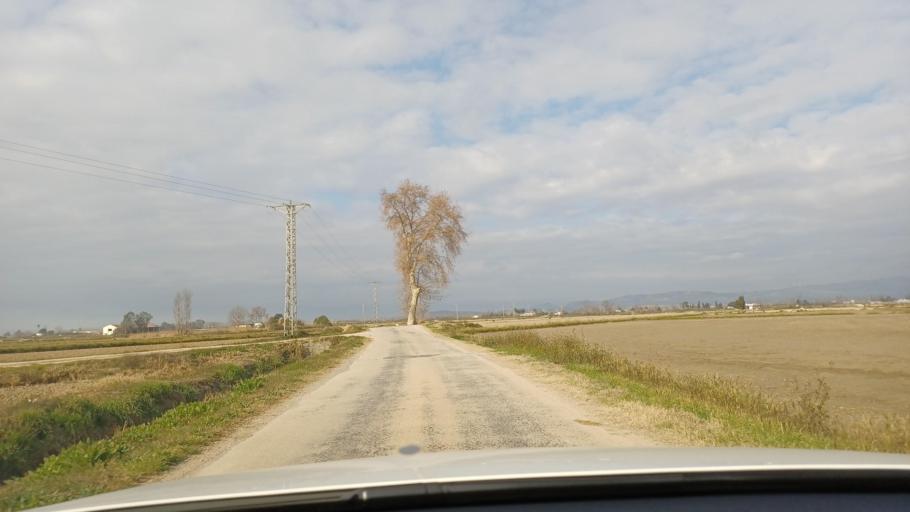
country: ES
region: Catalonia
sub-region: Provincia de Tarragona
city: Amposta
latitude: 40.7019
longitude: 0.6390
